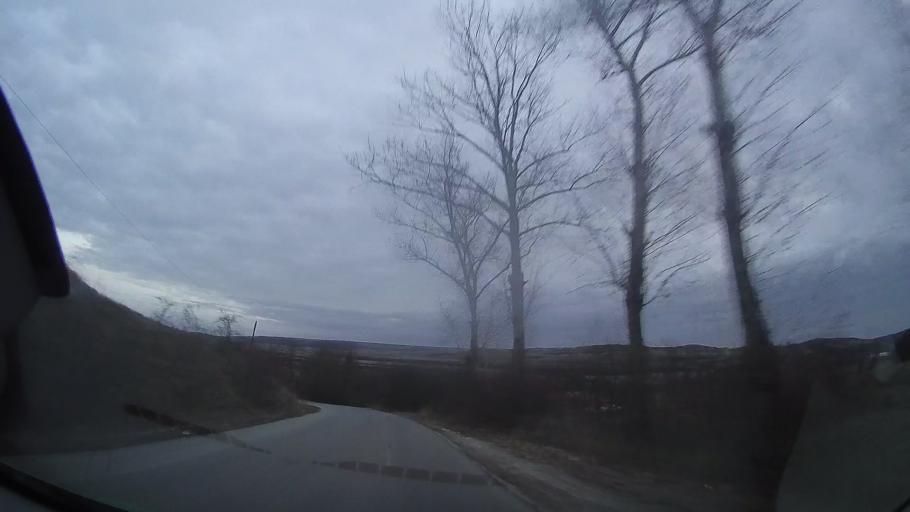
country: RO
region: Cluj
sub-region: Comuna Caianu
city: Caianu
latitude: 46.8035
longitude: 23.9303
